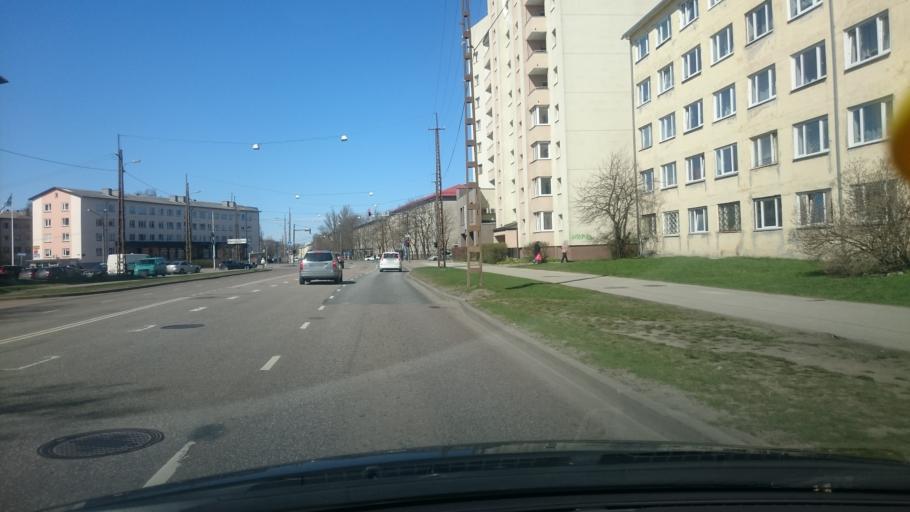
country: EE
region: Harju
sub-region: Tallinna linn
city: Tallinn
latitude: 59.4482
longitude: 24.6990
